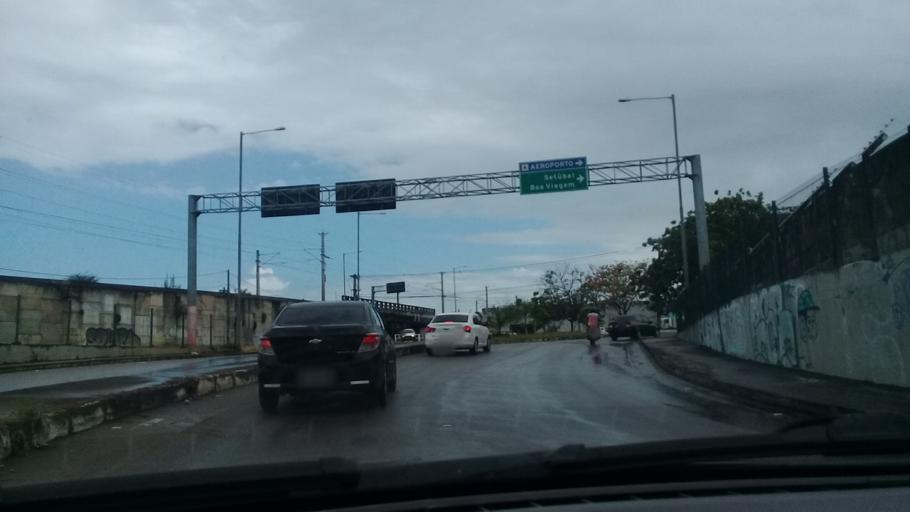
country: BR
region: Pernambuco
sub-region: Jaboatao Dos Guararapes
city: Jaboatao
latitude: -8.1426
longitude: -34.9171
